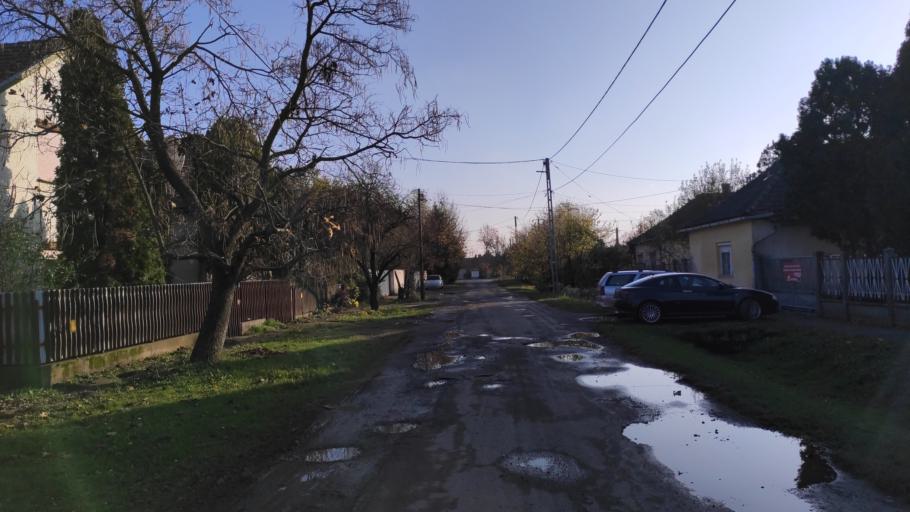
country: HU
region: Bekes
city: Mezobereny
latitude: 46.7623
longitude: 21.0448
